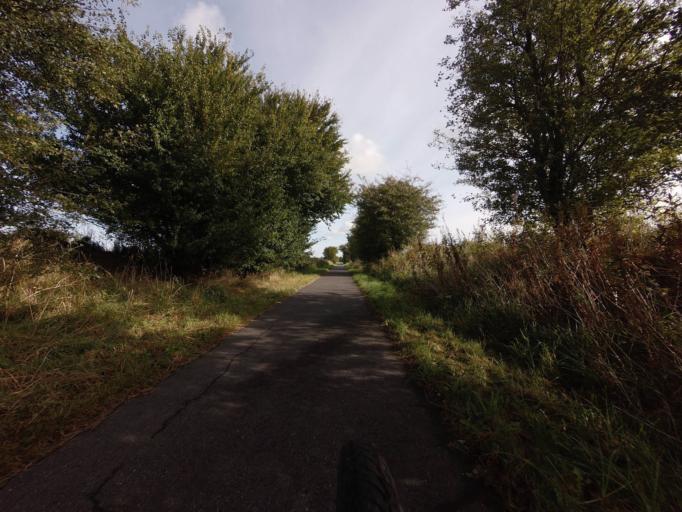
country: DK
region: Central Jutland
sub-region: Viborg Kommune
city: Bjerringbro
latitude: 56.4750
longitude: 9.6033
